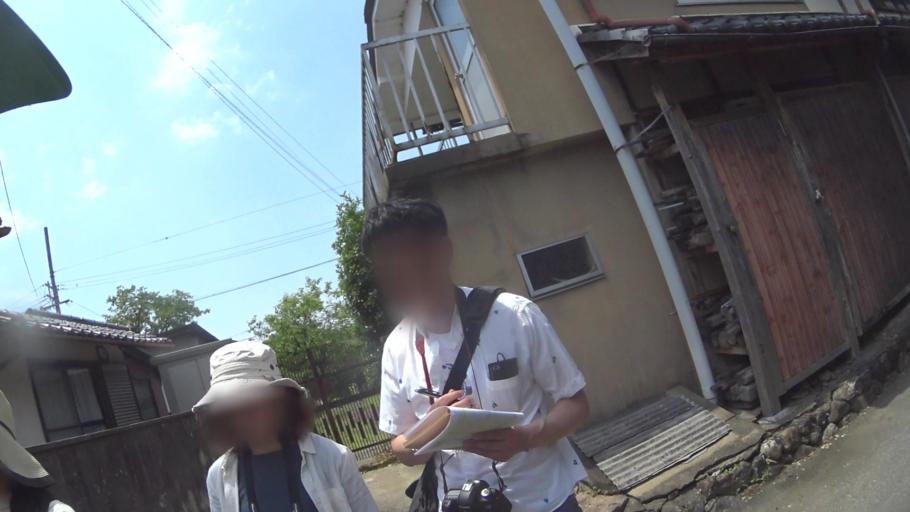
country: JP
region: Kyoto
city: Kameoka
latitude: 35.0345
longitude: 135.5676
